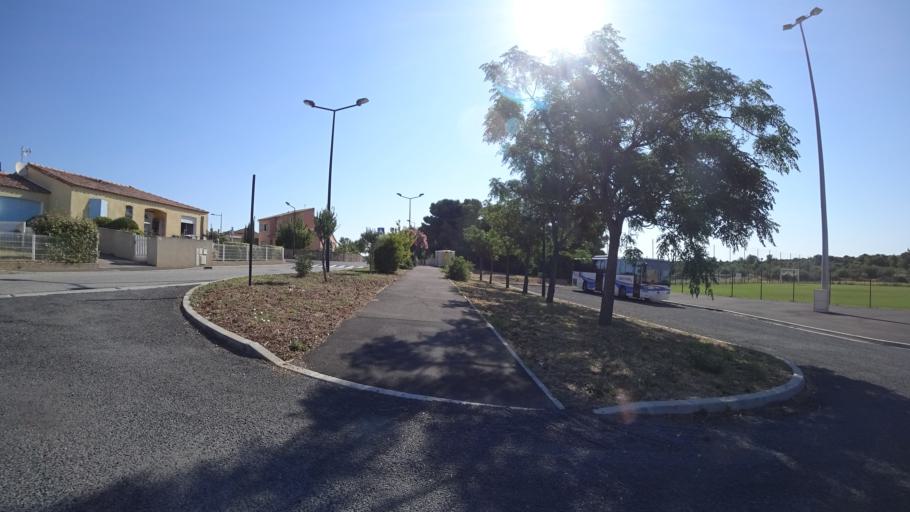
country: FR
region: Languedoc-Roussillon
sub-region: Departement de l'Aude
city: Leucate
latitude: 42.9048
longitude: 3.0336
